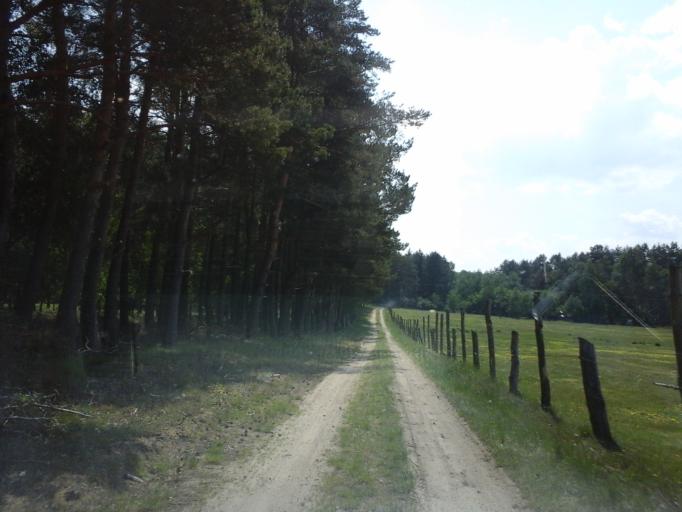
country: PL
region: West Pomeranian Voivodeship
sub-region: Powiat choszczenski
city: Drawno
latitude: 53.2444
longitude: 15.6678
